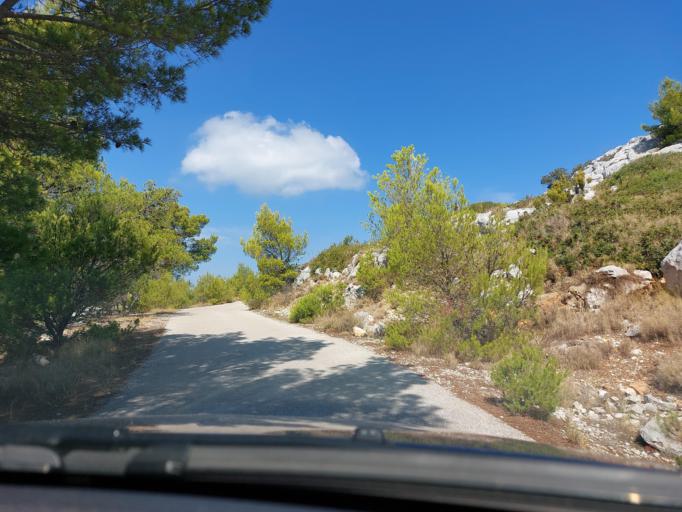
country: HR
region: Dubrovacko-Neretvanska
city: Smokvica
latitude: 42.7439
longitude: 16.8559
